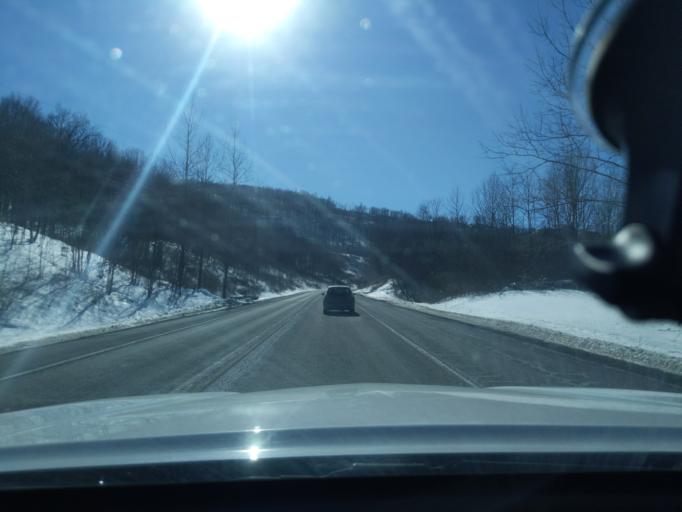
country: US
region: Maryland
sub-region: Allegany County
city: Lonaconing
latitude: 39.5437
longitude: -79.0032
